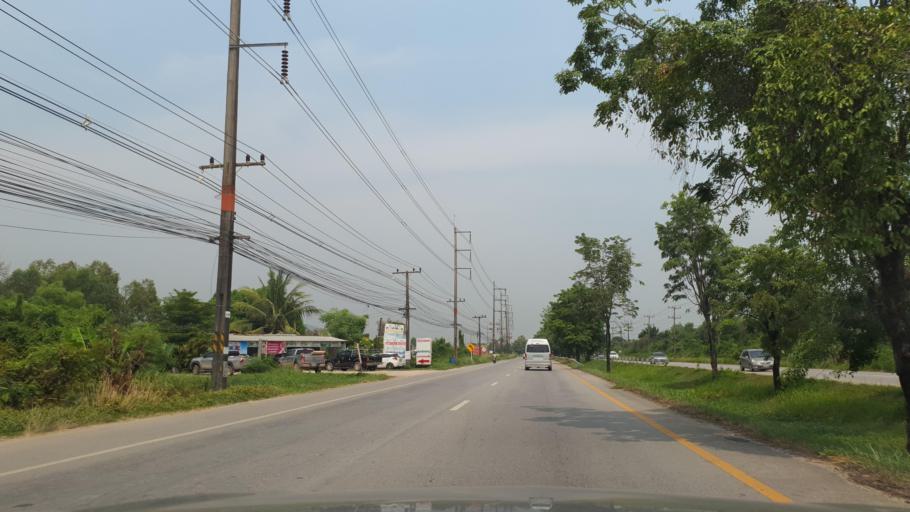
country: TH
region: Rayong
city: Rayong
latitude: 12.6392
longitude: 101.3690
